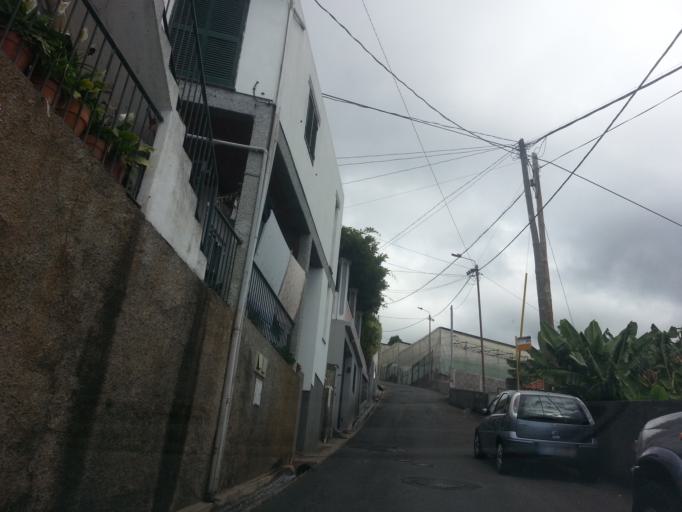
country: PT
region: Madeira
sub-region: Funchal
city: Nossa Senhora do Monte
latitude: 32.6674
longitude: -16.9309
